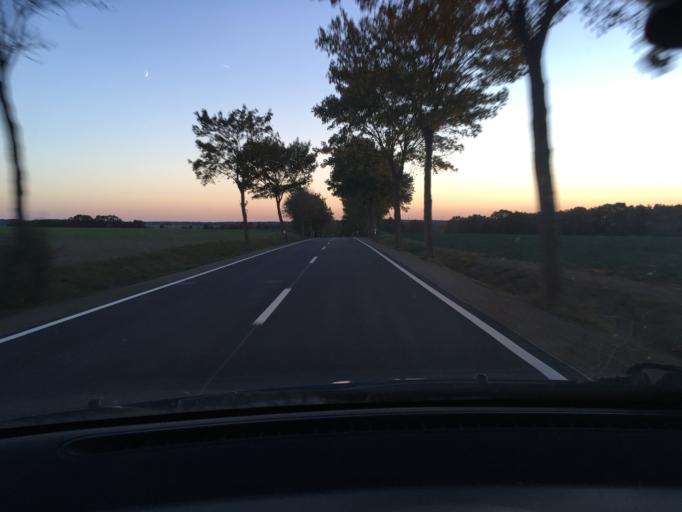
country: DE
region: Lower Saxony
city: Reinstorf
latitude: 53.2467
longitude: 10.5940
